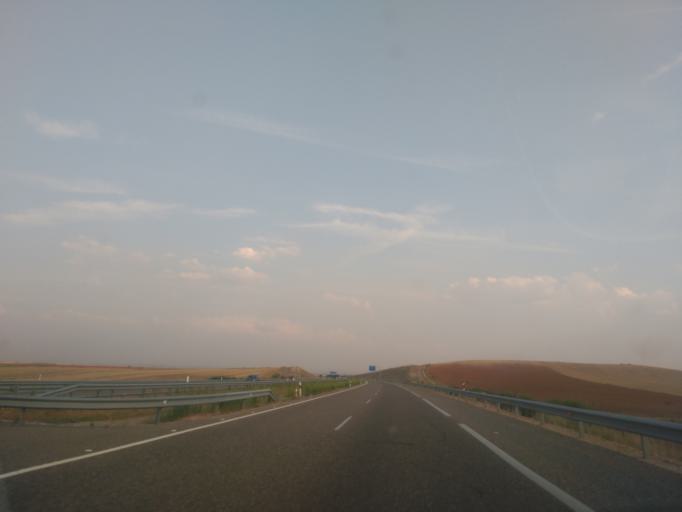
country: ES
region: Castille and Leon
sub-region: Provincia de Zamora
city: Roales
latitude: 41.5664
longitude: -5.7667
